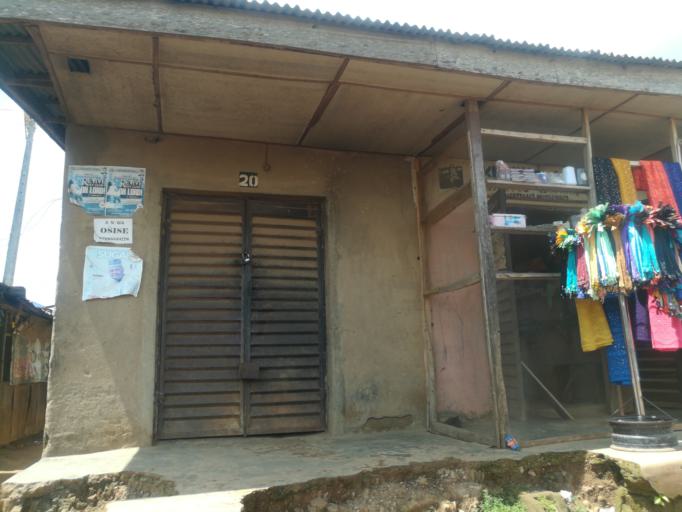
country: NG
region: Oyo
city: Lalupon
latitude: 7.4359
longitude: 4.0053
